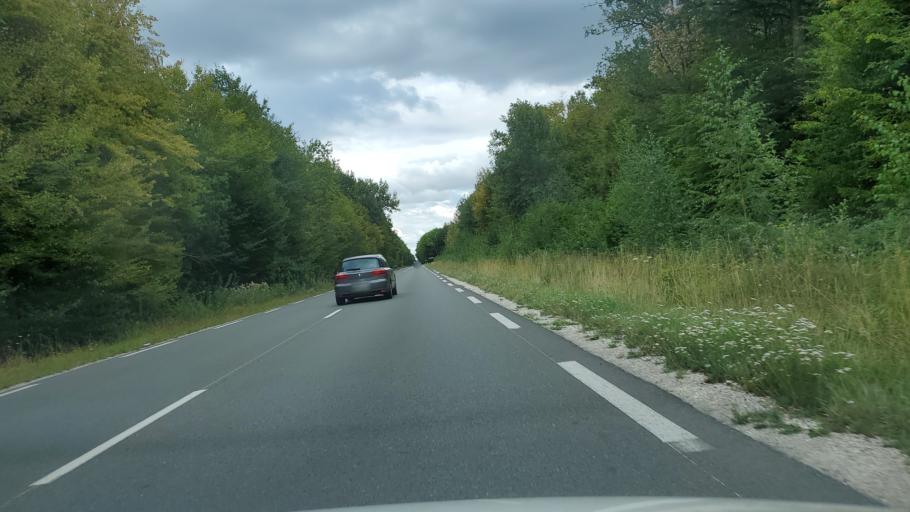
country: FR
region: Ile-de-France
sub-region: Departement de Seine-et-Marne
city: Mortcerf
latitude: 48.7699
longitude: 2.9108
